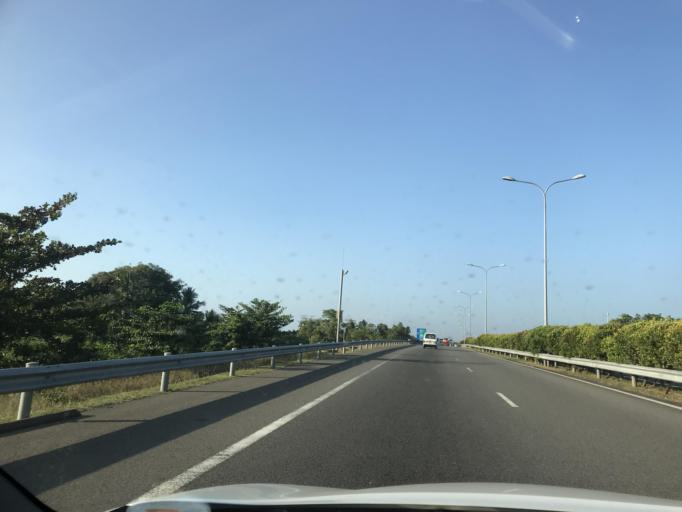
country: LK
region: Western
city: Ja Ela
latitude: 7.0752
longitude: 79.8777
